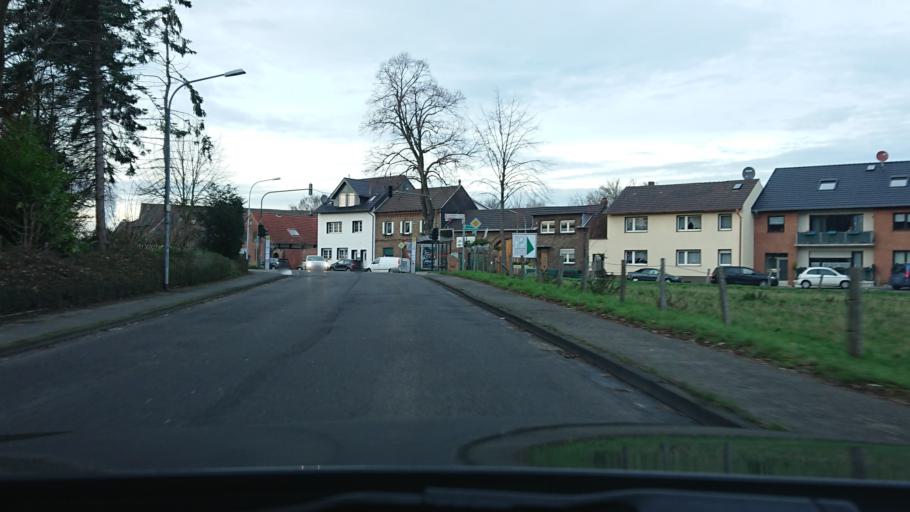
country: DE
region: North Rhine-Westphalia
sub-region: Regierungsbezirk Koln
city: Pulheim
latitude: 50.9922
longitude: 6.7430
